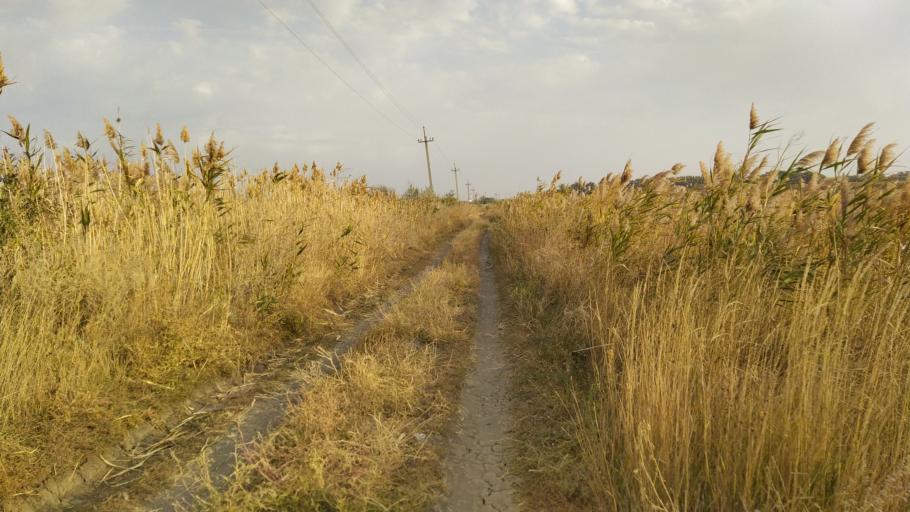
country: RU
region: Rostov
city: Kuleshovka
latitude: 47.1131
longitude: 39.6071
